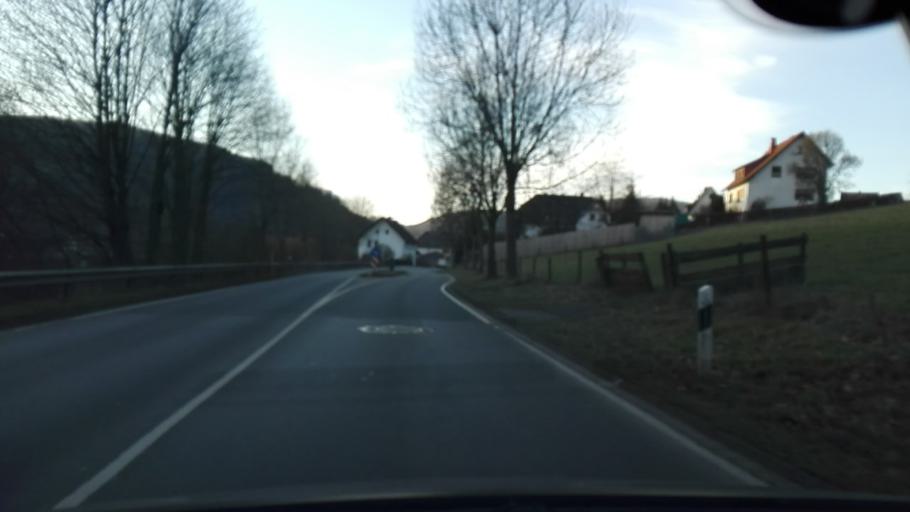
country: DE
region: North Rhine-Westphalia
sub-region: Regierungsbezirk Arnsberg
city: Finnentrop
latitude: 51.2122
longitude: 7.9657
